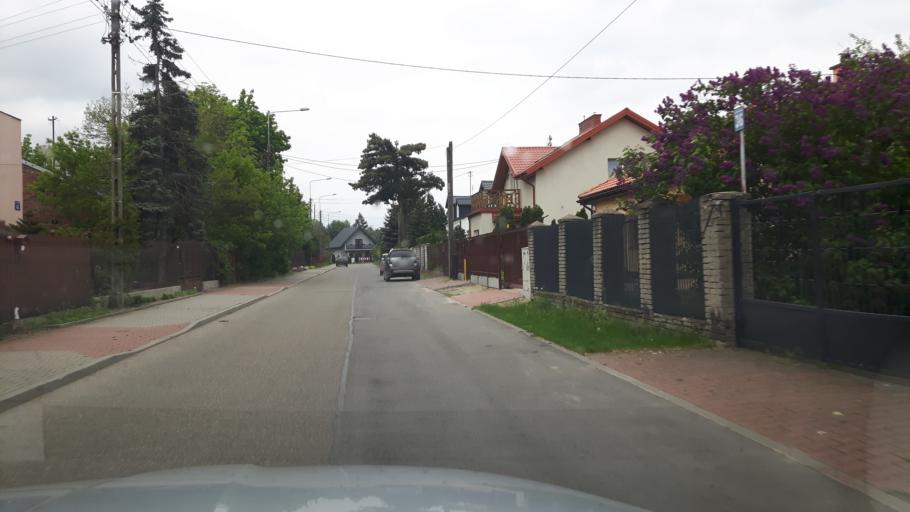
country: PL
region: Masovian Voivodeship
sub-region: Warszawa
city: Rembertow
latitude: 52.2501
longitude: 21.1689
